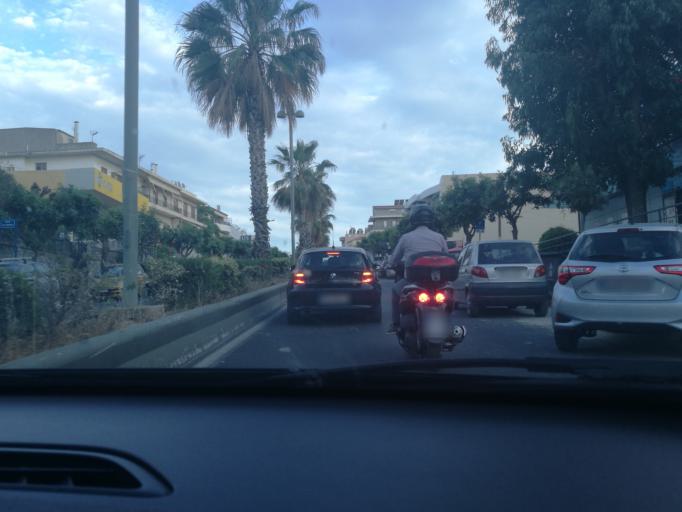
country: GR
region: Crete
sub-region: Nomos Irakleiou
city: Irakleion
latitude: 35.3186
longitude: 25.1447
